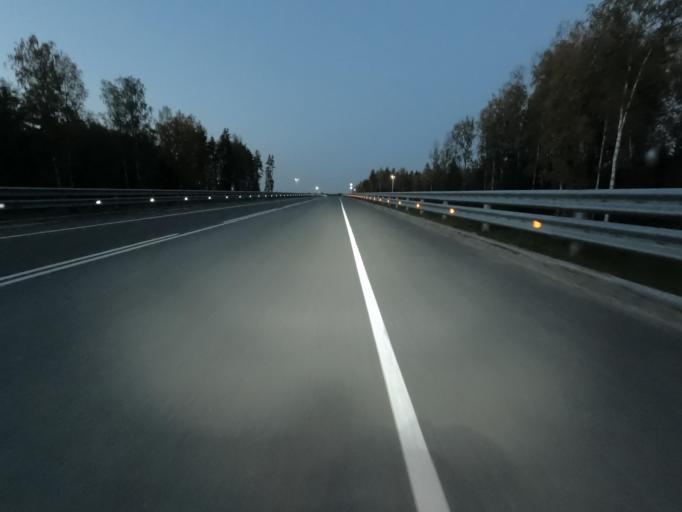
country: RU
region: Leningrad
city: Lyuban'
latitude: 59.1964
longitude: 31.2557
